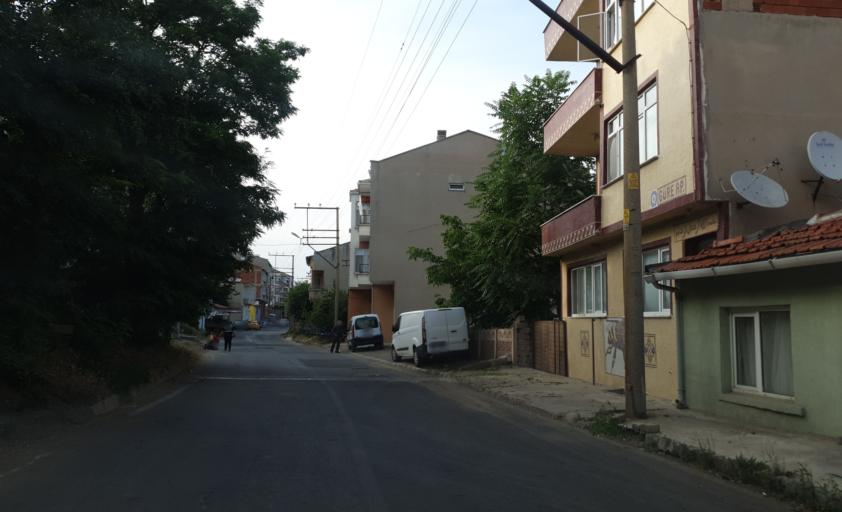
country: TR
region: Tekirdag
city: Hayrabolu
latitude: 41.2147
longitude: 27.1100
